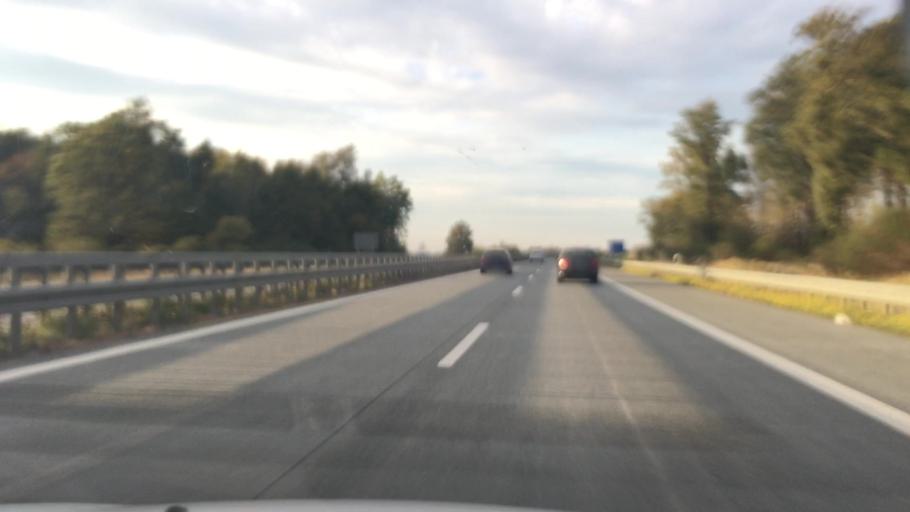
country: DE
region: Saxony
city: Schonfeld
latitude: 51.3212
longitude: 13.7209
